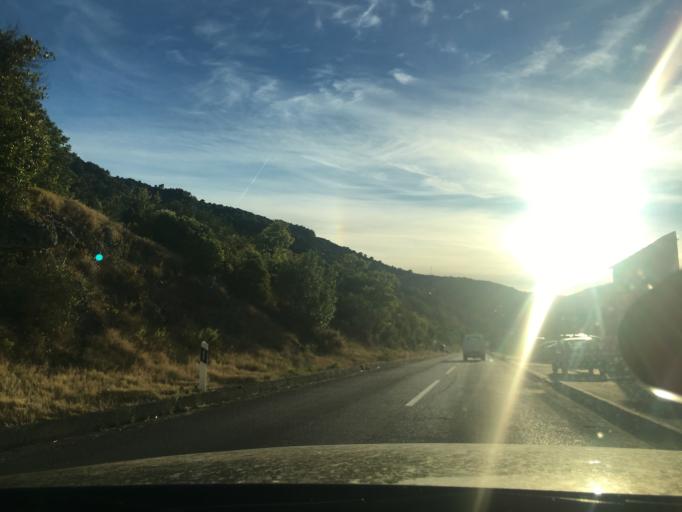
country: HR
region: Splitsko-Dalmatinska
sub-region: Grad Vis
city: Vis
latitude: 43.0586
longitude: 16.1842
